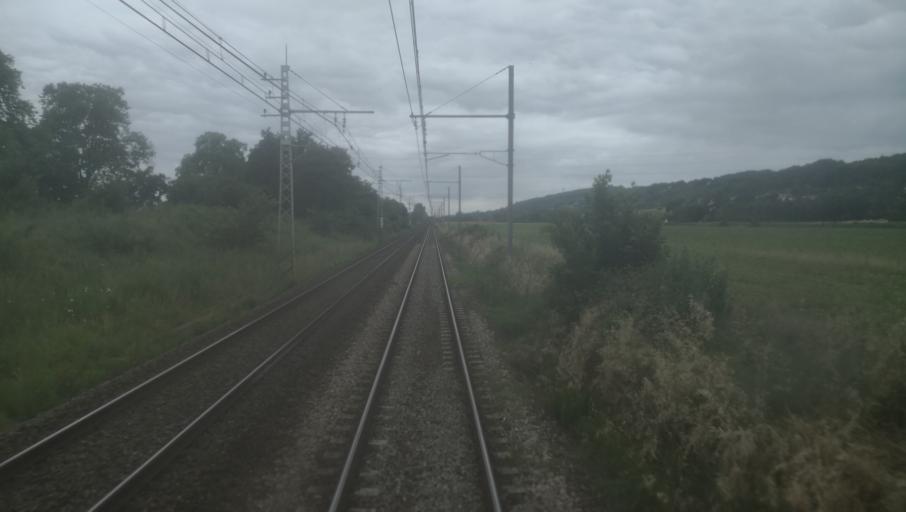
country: FR
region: Midi-Pyrenees
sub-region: Departement de la Haute-Garonne
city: Castelnau-d'Estretefonds
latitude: 43.7896
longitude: 1.3384
